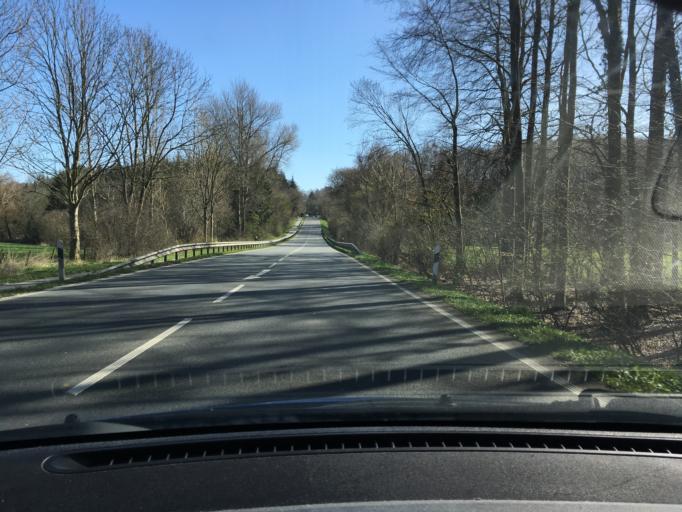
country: DE
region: Schleswig-Holstein
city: Guby
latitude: 54.4815
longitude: 9.6819
